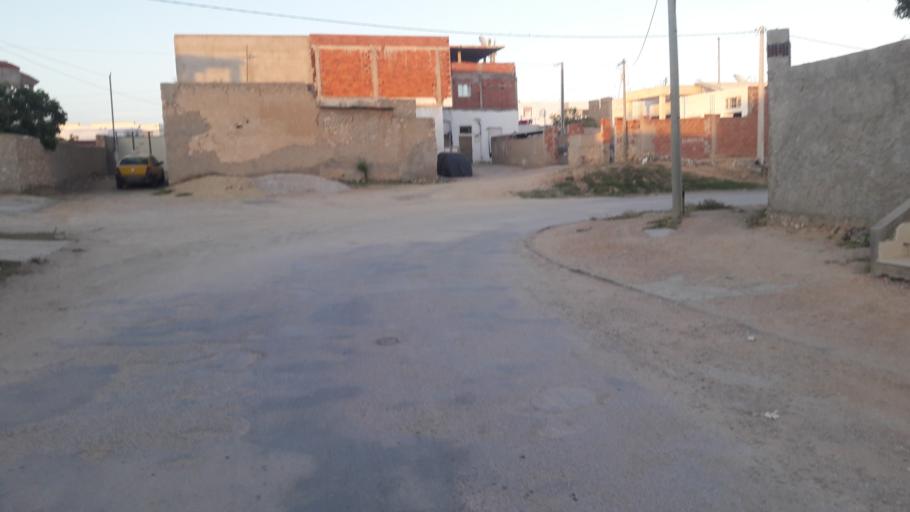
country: TN
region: Safaqis
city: Al Qarmadah
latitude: 34.8088
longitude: 10.7487
